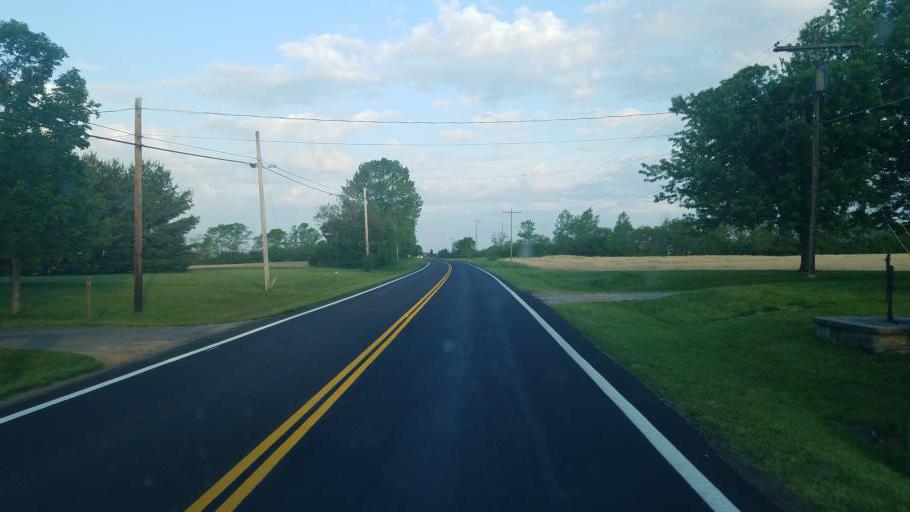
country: US
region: Ohio
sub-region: Highland County
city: Greenfield
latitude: 39.3547
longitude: -83.4453
